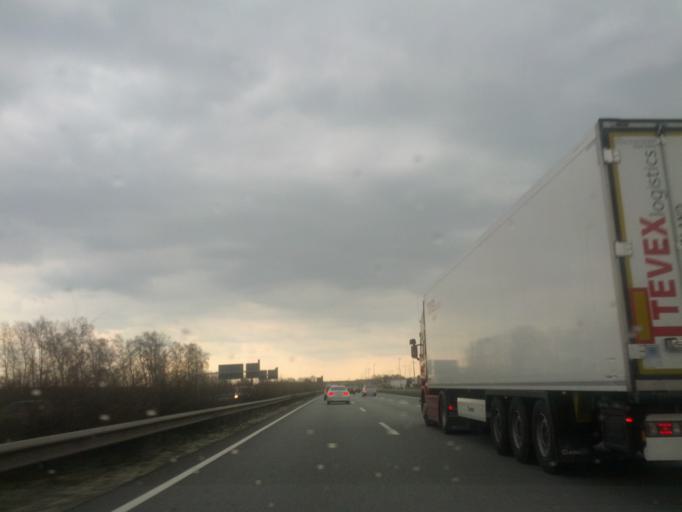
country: DE
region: Lower Saxony
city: Langwedel
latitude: 52.9995
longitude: 9.1807
